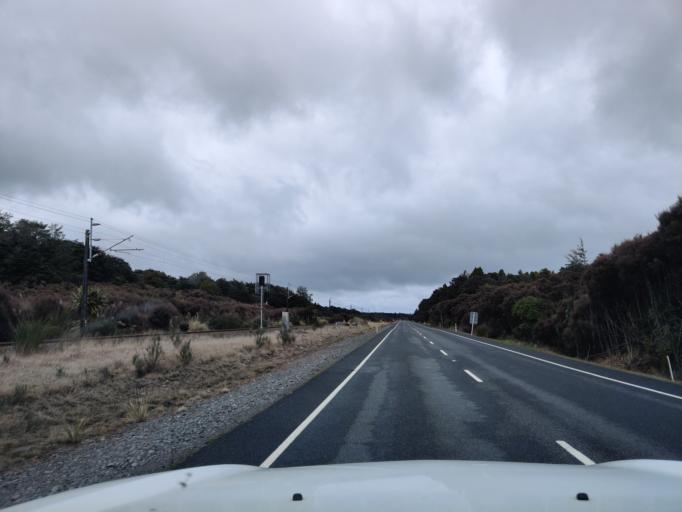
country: NZ
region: Manawatu-Wanganui
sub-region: Ruapehu District
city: Waiouru
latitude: -39.3156
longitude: 175.3875
